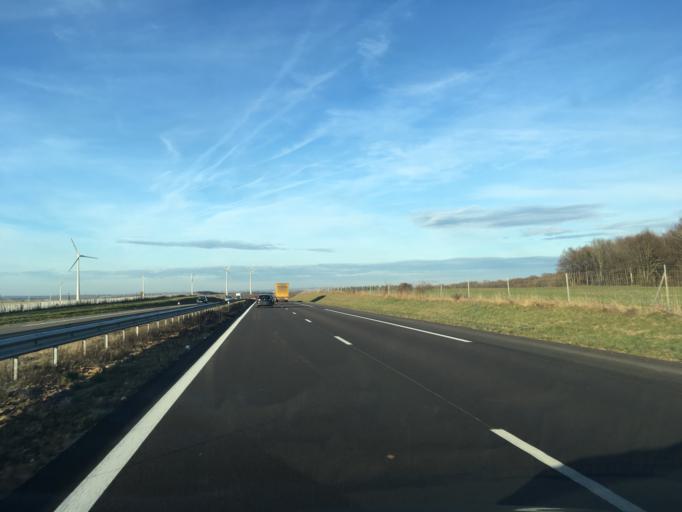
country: FR
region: Bourgogne
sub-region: Departement de l'Yonne
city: Joux-la-Ville
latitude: 47.6181
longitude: 3.9090
